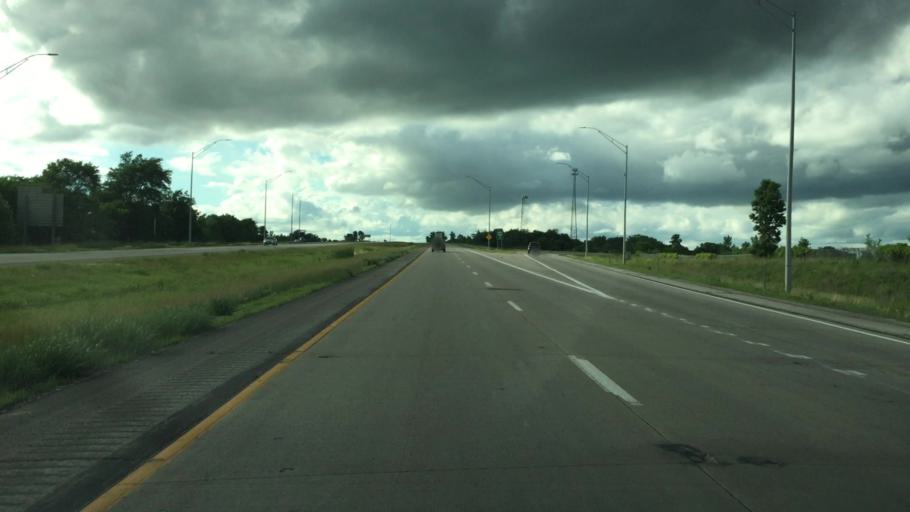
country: US
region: Iowa
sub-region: Polk County
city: Altoona
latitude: 41.6550
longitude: -93.5178
